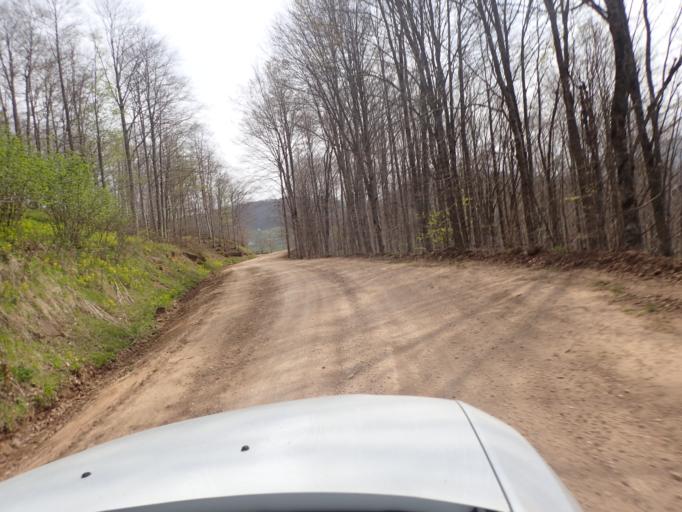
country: TR
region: Ordu
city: Aybasti
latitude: 40.7053
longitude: 37.2849
